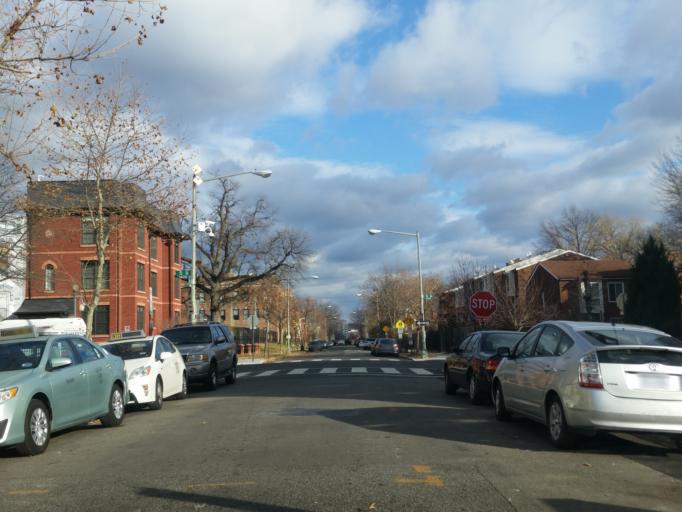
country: US
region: Washington, D.C.
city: Washington, D.C.
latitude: 38.9086
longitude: -77.0193
